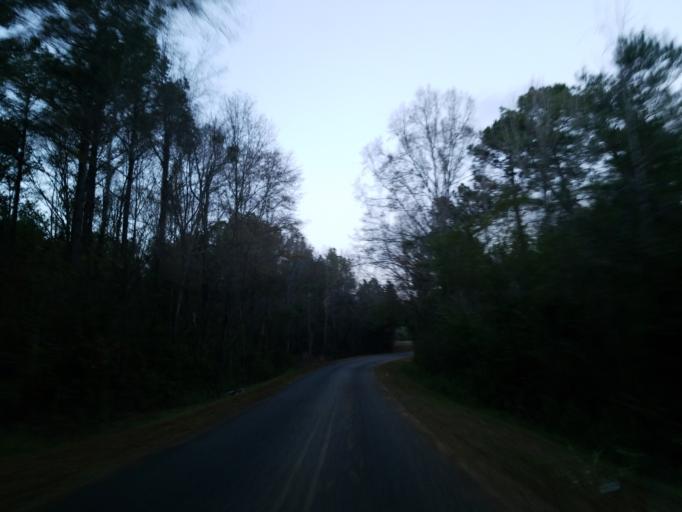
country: US
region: Alabama
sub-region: Sumter County
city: York
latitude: 32.4034
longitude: -88.4598
